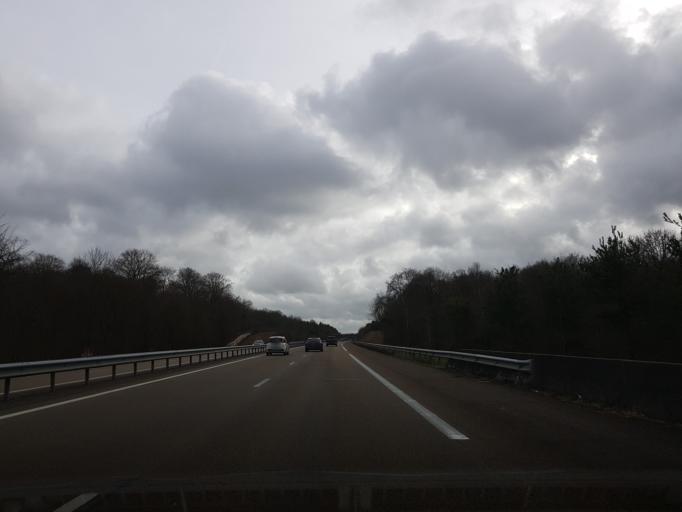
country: FR
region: Champagne-Ardenne
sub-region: Departement de la Haute-Marne
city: Chamarandes-Choignes
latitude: 48.0238
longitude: 5.0920
